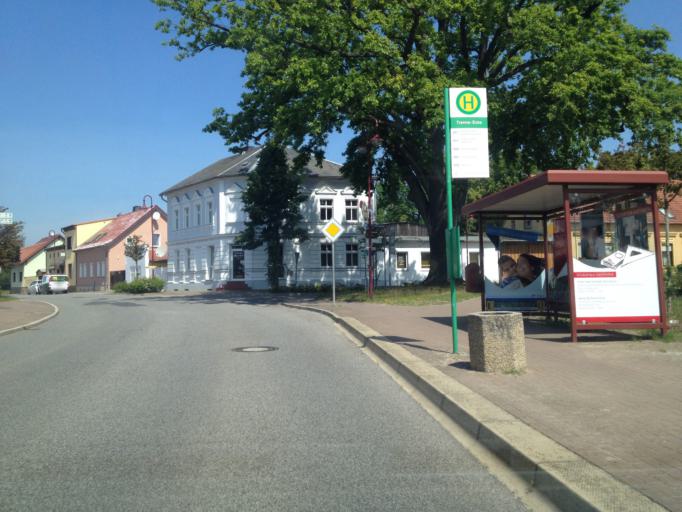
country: DE
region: Brandenburg
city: Joachimsthal
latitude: 52.9767
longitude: 13.7533
